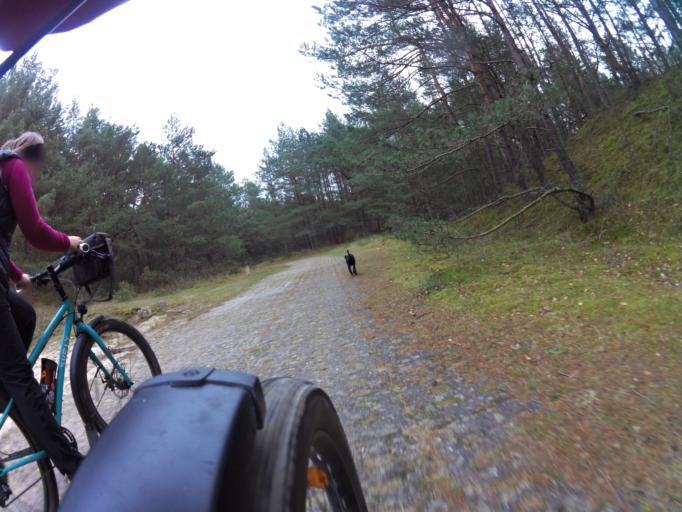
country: PL
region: Pomeranian Voivodeship
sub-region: Powiat leborski
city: Leba
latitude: 54.7686
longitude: 17.5960
